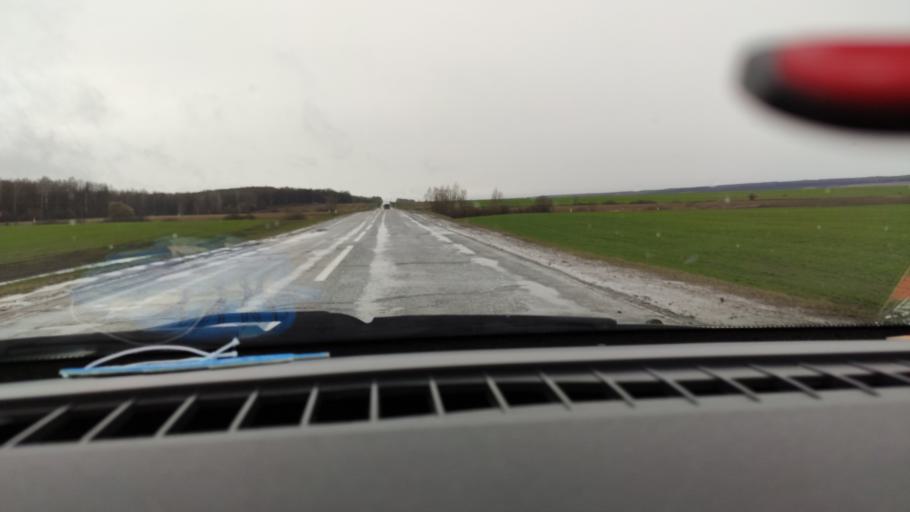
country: RU
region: Samara
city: Chelno-Vershiny
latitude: 54.6300
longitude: 50.9595
